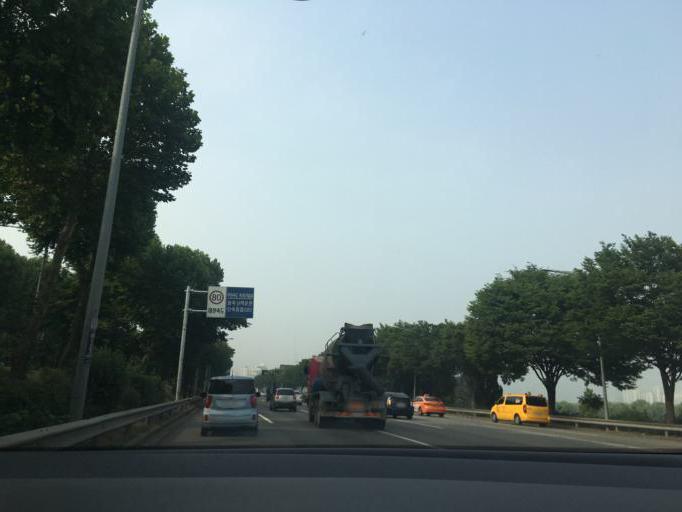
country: KR
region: Gyeonggi-do
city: Guri-si
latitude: 37.5524
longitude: 127.1235
